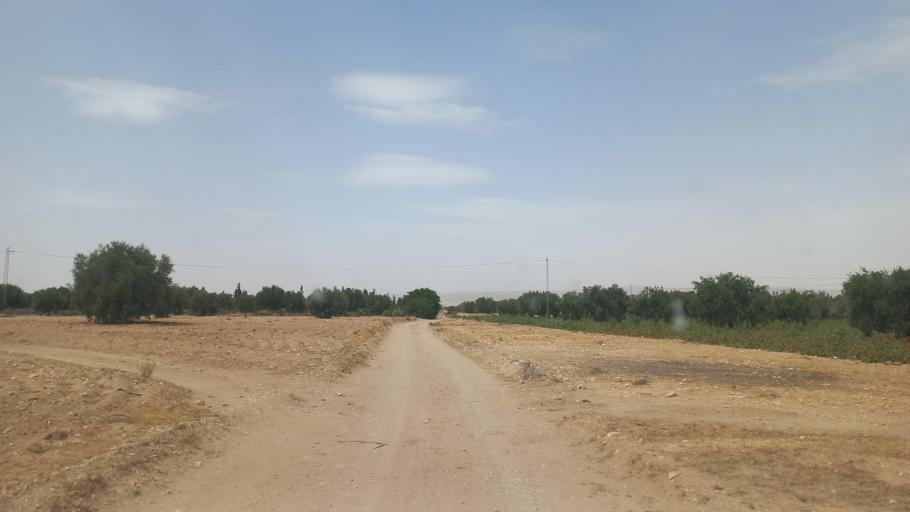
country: TN
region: Al Qasrayn
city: Kasserine
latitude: 35.2571
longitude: 9.0030
